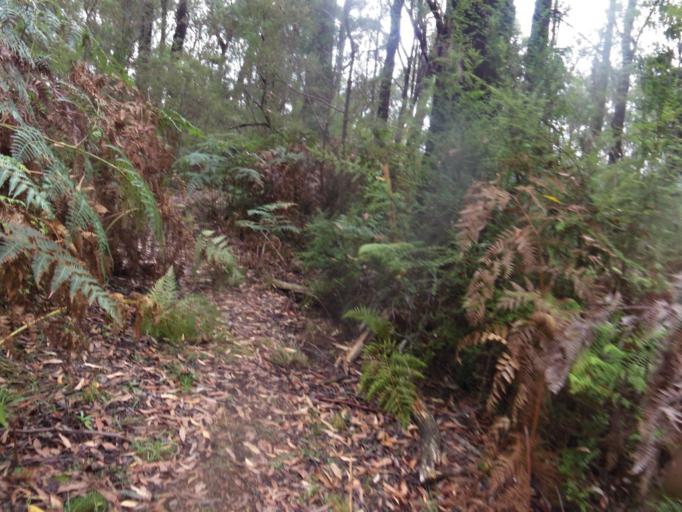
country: AU
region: Victoria
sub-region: Nillumbik
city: Saint Andrews
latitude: -37.5375
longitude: 145.3495
